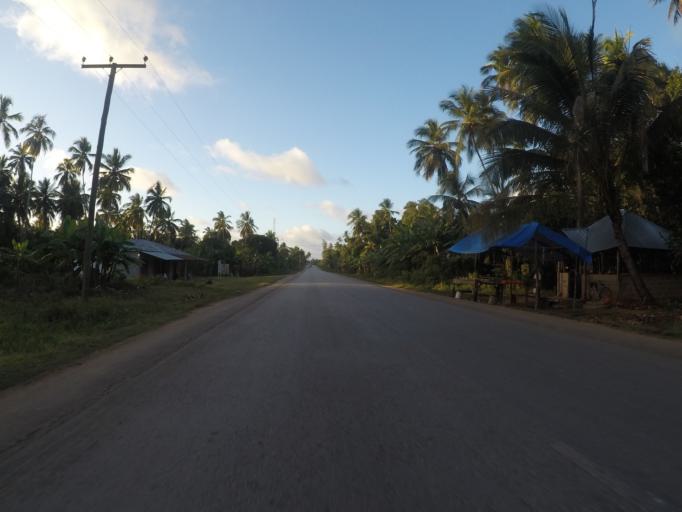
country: TZ
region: Zanzibar Central/South
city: Koani
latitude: -6.1264
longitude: 39.3259
